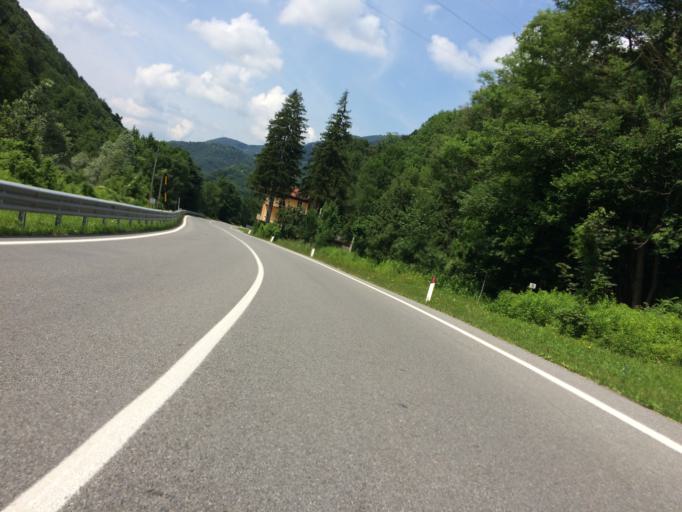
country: IT
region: Piedmont
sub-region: Provincia di Cuneo
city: Limone Piemonte
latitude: 44.2128
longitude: 7.5727
